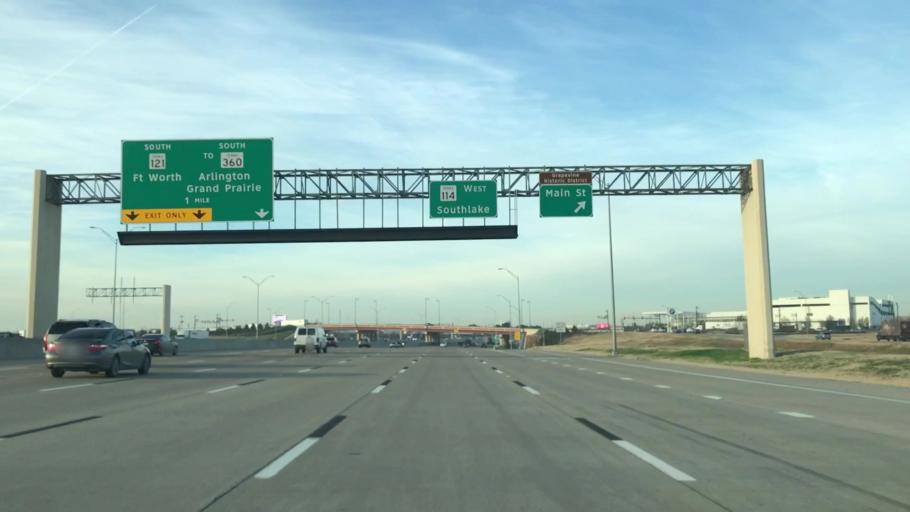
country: US
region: Texas
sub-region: Tarrant County
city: Grapevine
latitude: 32.9255
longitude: -97.0572
